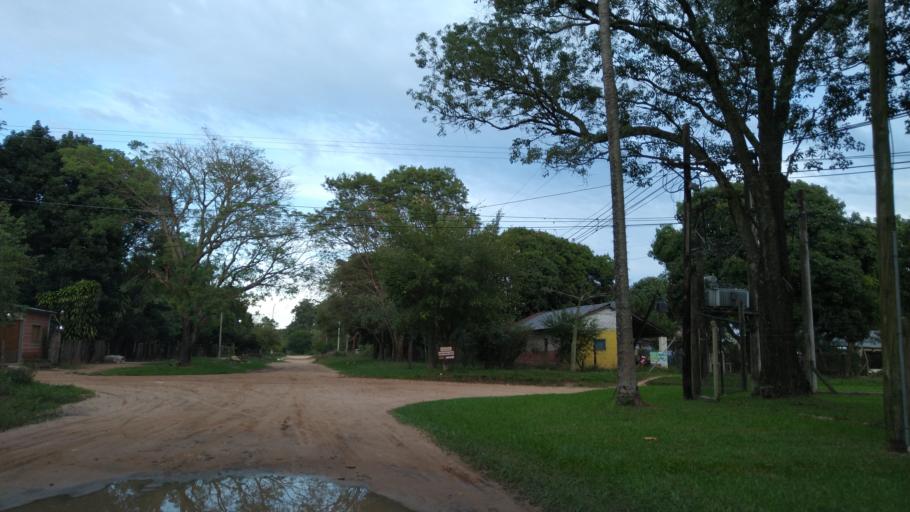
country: AR
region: Corrientes
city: Ituzaingo
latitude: -27.5937
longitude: -56.7077
